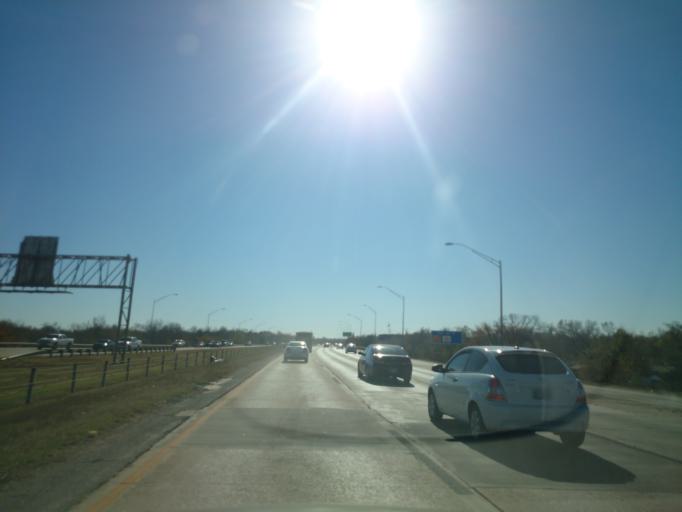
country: US
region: Oklahoma
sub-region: Oklahoma County
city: Oklahoma City
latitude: 35.4469
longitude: -97.5701
